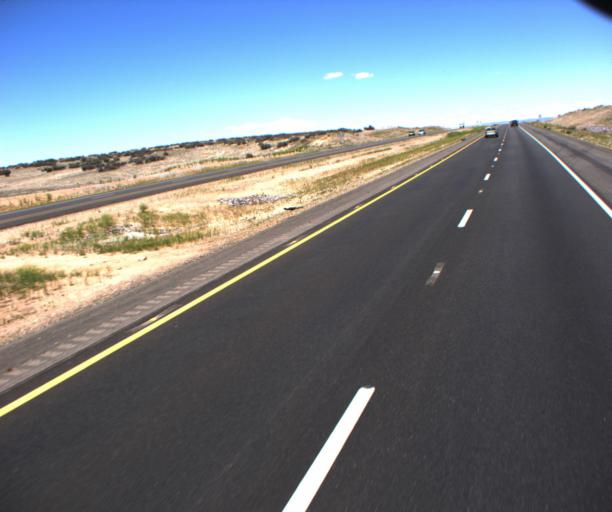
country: US
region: Arizona
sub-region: Yavapai County
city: Chino Valley
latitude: 34.6606
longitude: -112.4370
